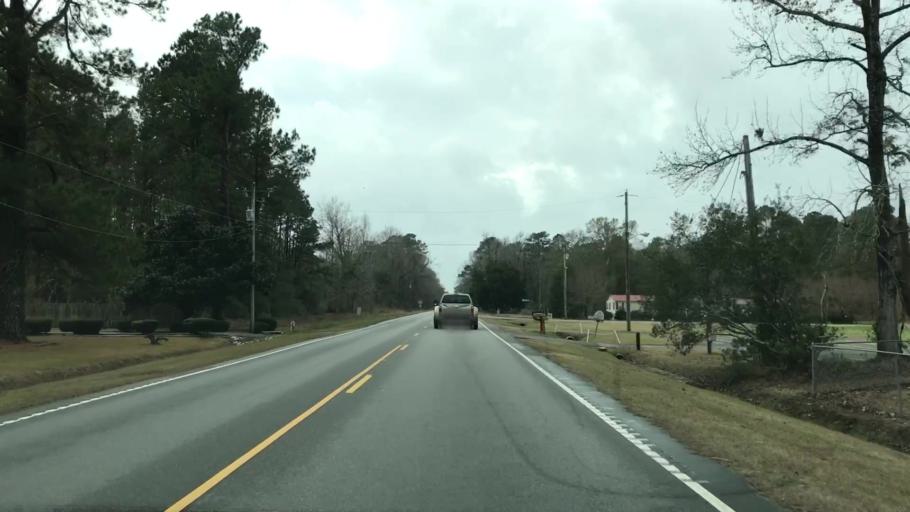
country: US
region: South Carolina
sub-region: Horry County
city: Socastee
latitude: 33.6899
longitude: -79.1187
